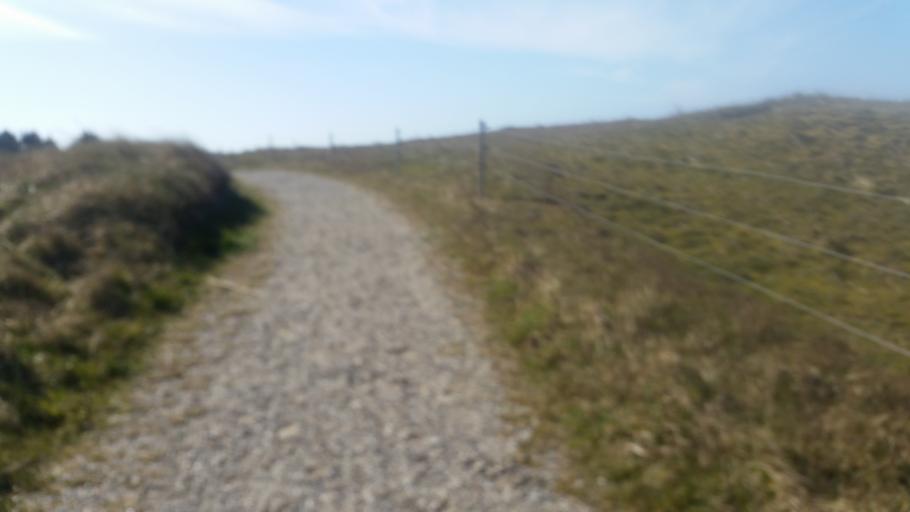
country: DE
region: Schleswig-Holstein
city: List
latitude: 55.1536
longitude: 8.5099
